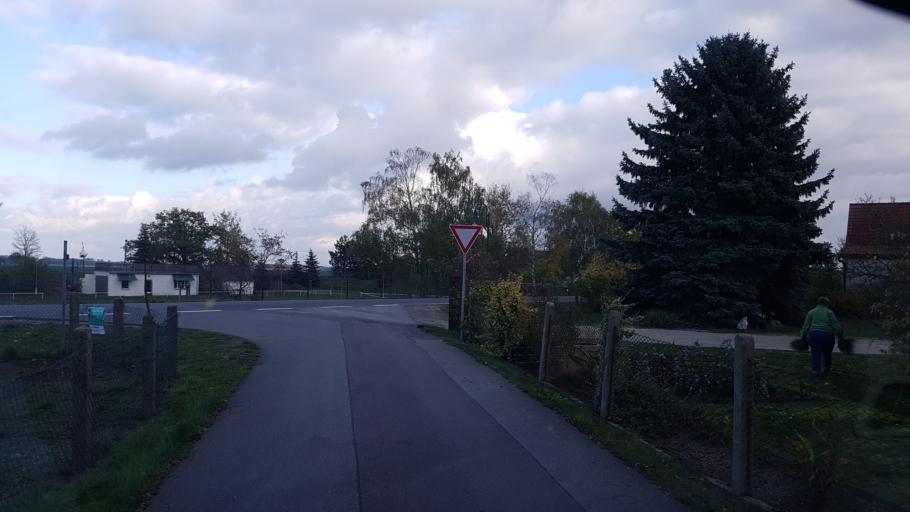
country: DE
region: Brandenburg
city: Doberlug-Kirchhain
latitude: 51.6545
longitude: 13.5179
